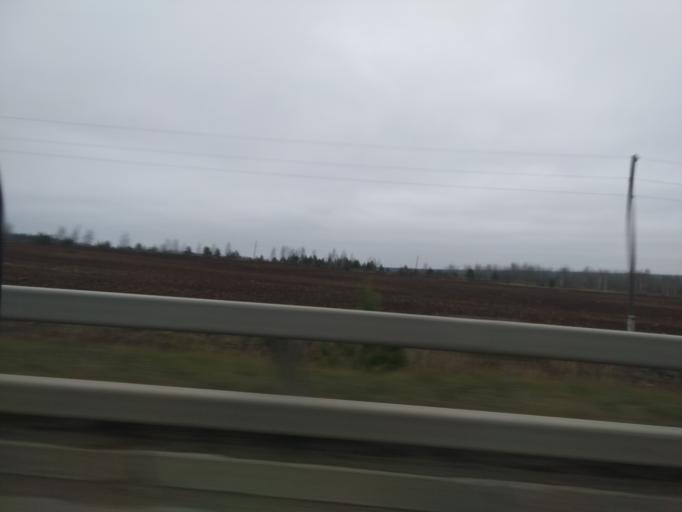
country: RU
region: Kirov
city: Krasnaya Polyana
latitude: 56.2276
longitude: 51.2072
